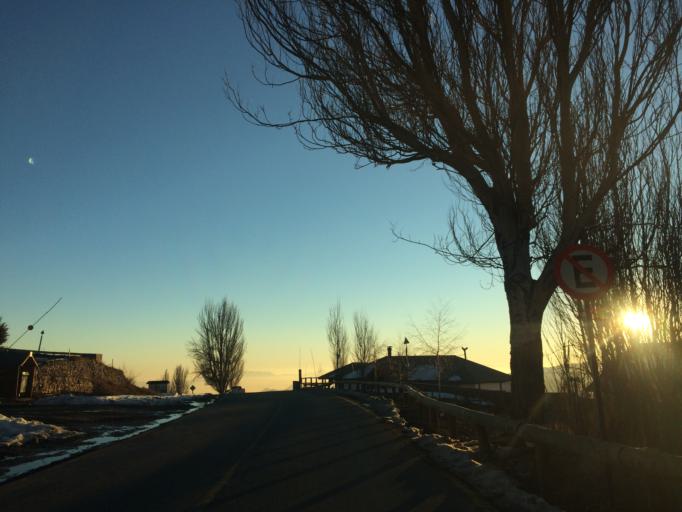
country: CL
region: Santiago Metropolitan
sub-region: Provincia de Santiago
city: Villa Presidente Frei, Nunoa, Santiago, Chile
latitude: -33.3445
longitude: -70.2999
